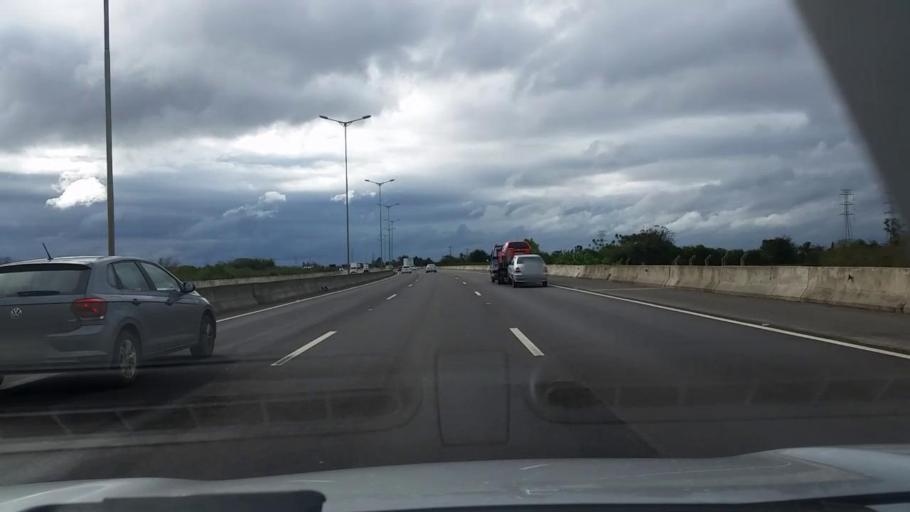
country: BR
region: Rio Grande do Sul
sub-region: Canoas
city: Canoas
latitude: -29.9434
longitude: -51.2047
